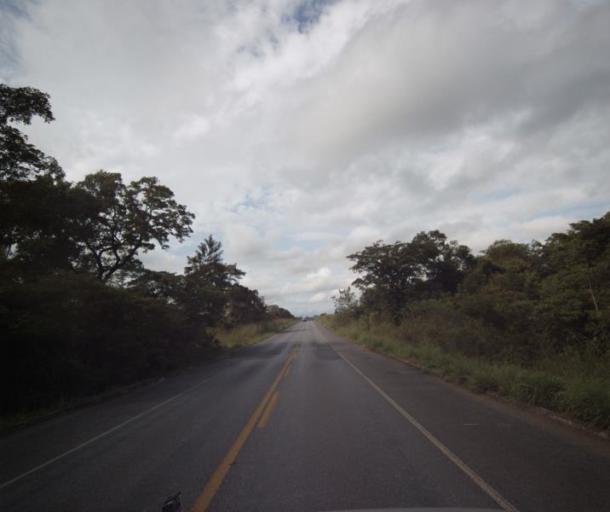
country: BR
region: Goias
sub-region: Pirenopolis
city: Pirenopolis
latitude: -15.5396
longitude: -48.6226
